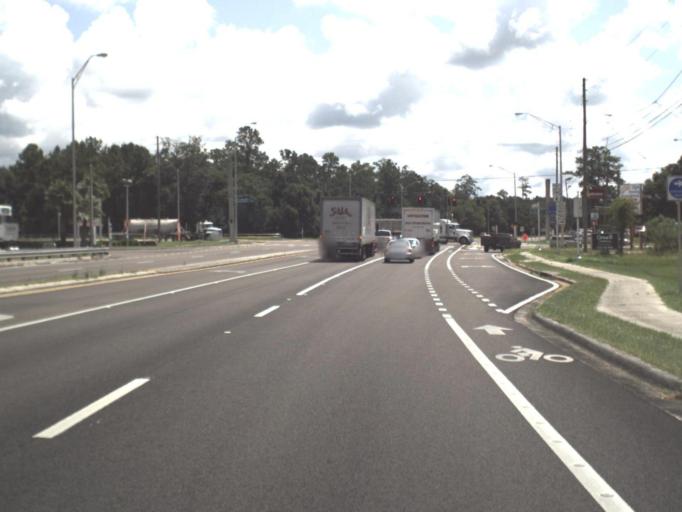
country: US
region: Florida
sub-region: Hernando County
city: North Brooksville
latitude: 28.5520
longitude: -82.4221
